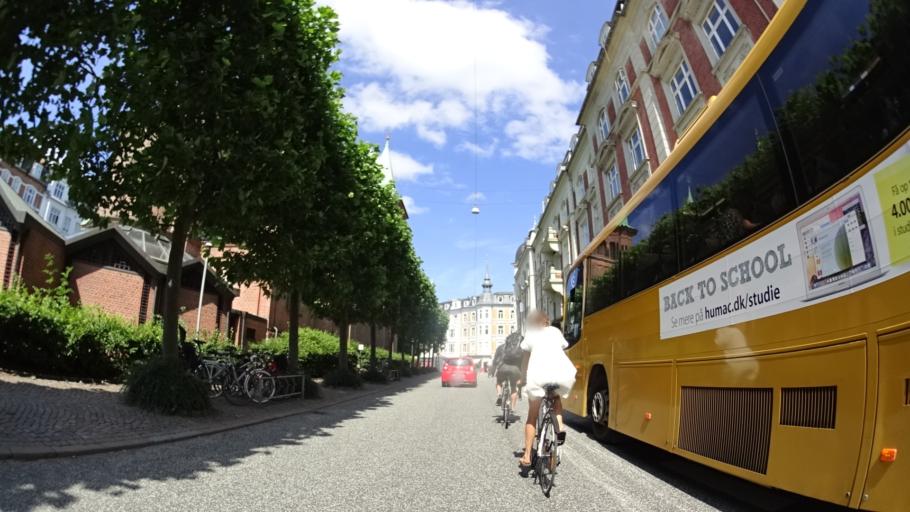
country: DK
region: Central Jutland
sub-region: Arhus Kommune
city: Arhus
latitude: 56.1458
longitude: 10.2043
